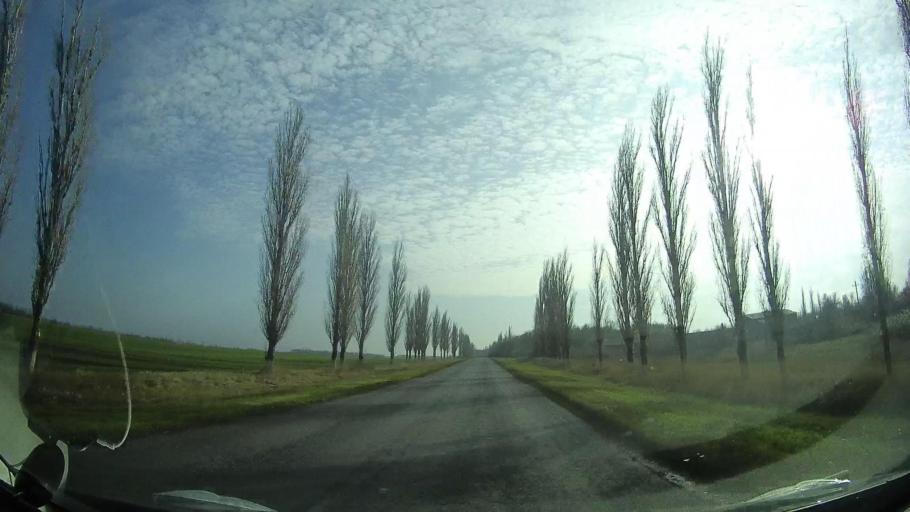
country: RU
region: Rostov
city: Mechetinskaya
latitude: 46.8292
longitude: 40.5518
